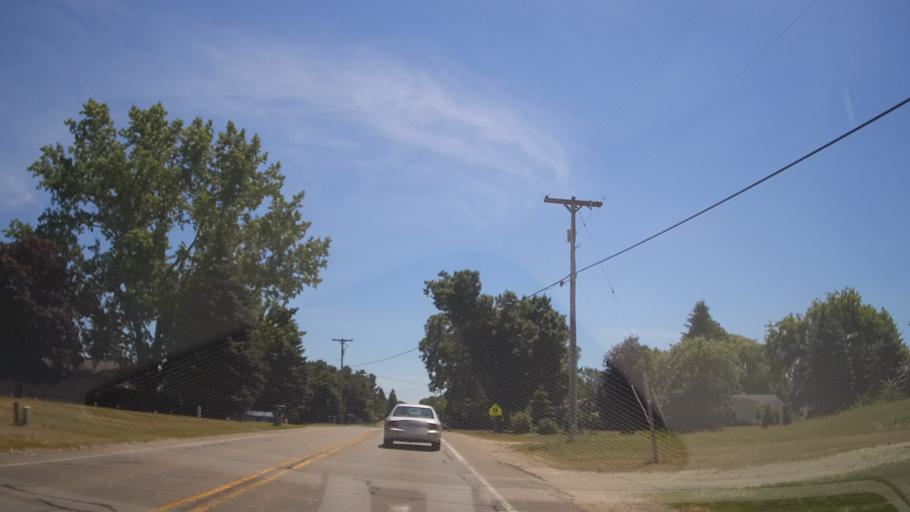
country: US
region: Michigan
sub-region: Grand Traverse County
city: Traverse City
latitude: 44.6962
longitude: -85.6918
